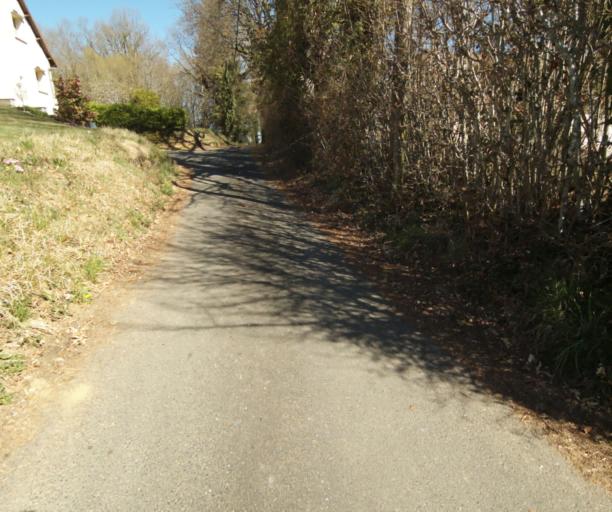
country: FR
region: Limousin
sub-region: Departement de la Correze
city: Chamboulive
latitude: 45.4337
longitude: 1.7155
